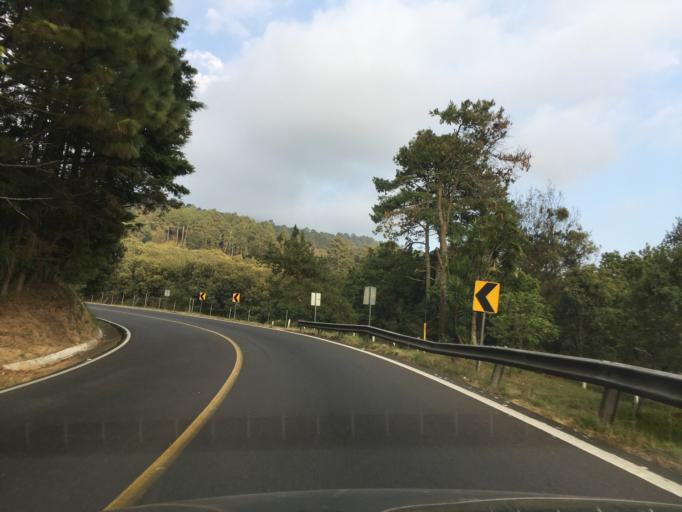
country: MX
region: Michoacan
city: Tingambato
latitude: 19.4920
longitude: -101.8334
